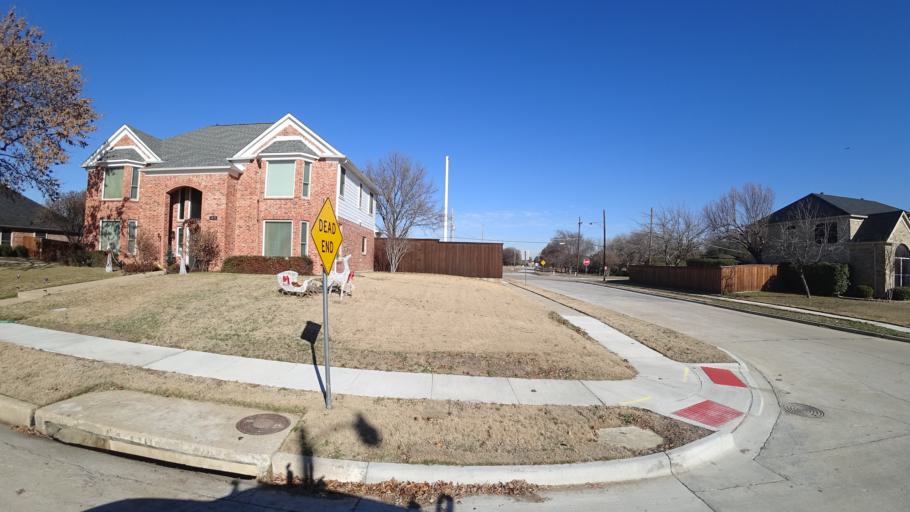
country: US
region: Texas
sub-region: Denton County
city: Lewisville
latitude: 33.0202
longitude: -97.0332
